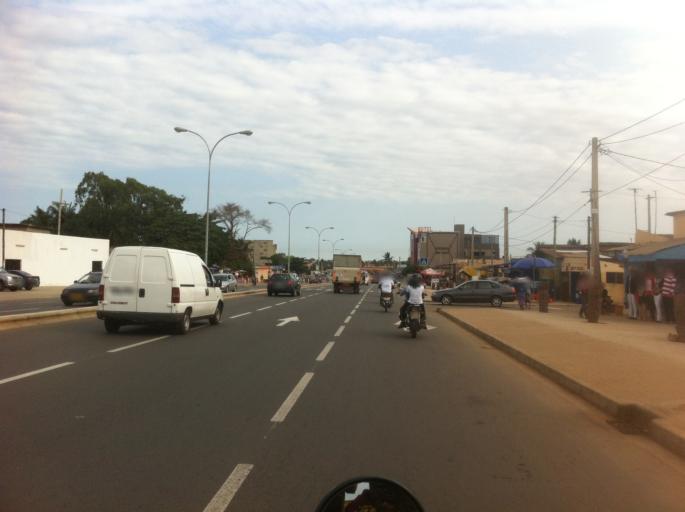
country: TG
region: Maritime
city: Lome
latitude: 6.1525
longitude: 1.2013
